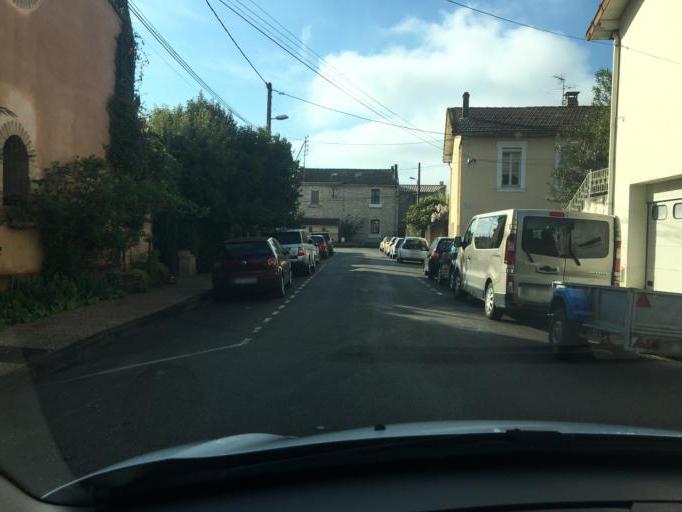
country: FR
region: Provence-Alpes-Cote d'Azur
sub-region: Departement du Vaucluse
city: Cavaillon
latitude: 43.8299
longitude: 5.0410
